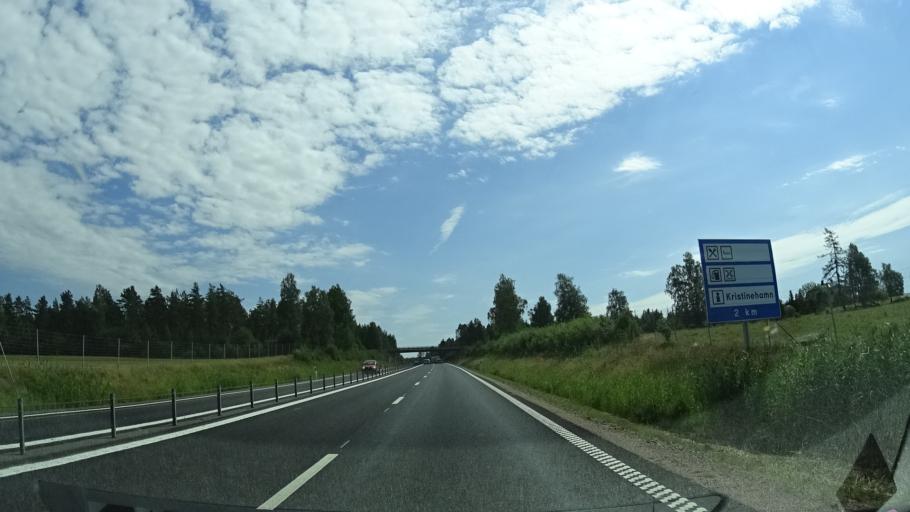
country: SE
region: Vaermland
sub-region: Karlstads Kommun
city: Skattkarr
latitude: 59.3938
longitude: 13.8207
